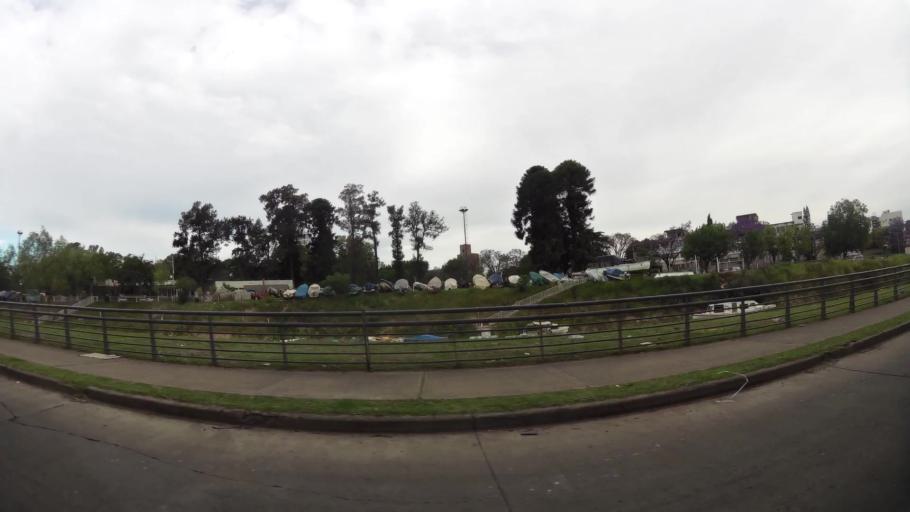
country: AR
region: Santa Fe
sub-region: Departamento de Rosario
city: Rosario
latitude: -32.9112
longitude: -60.6826
